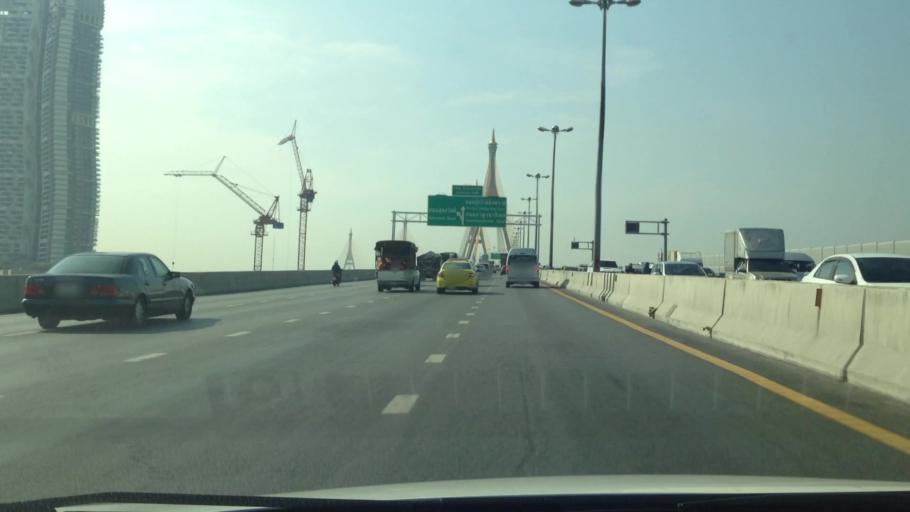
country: TH
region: Bangkok
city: Yan Nawa
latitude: 13.6776
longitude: 100.5395
